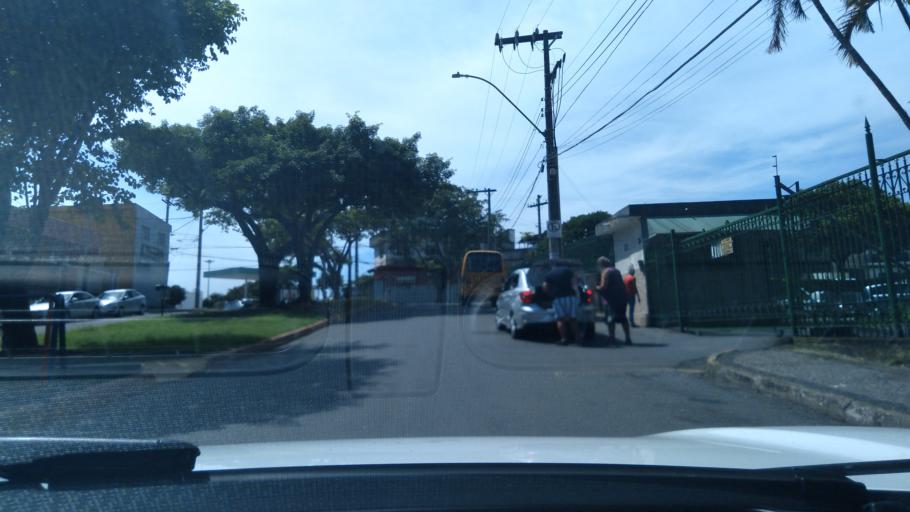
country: BR
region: Minas Gerais
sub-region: Contagem
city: Contagem
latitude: -19.9238
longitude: -44.0068
